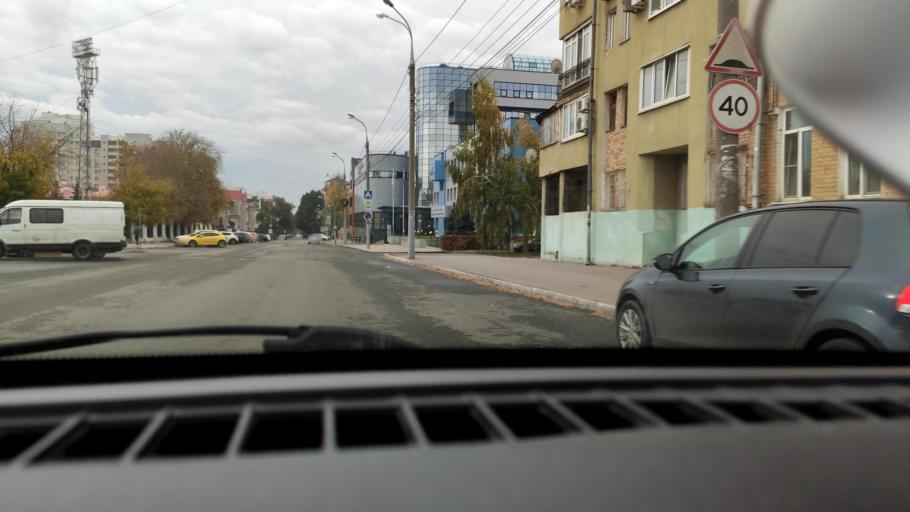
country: RU
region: Samara
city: Samara
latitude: 53.1881
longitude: 50.1071
